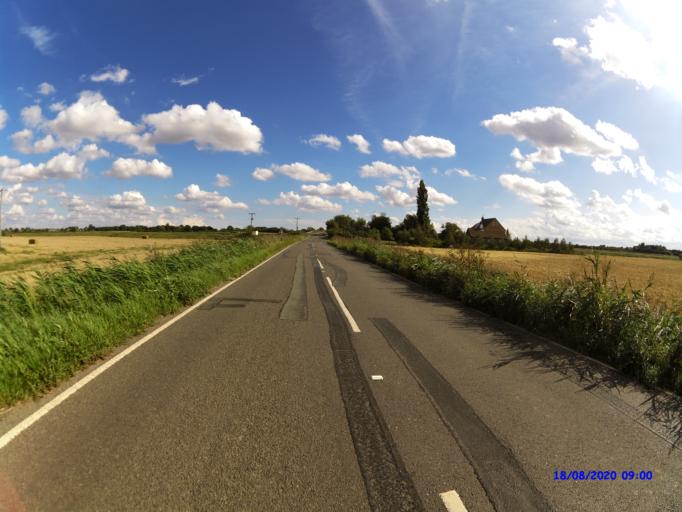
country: GB
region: England
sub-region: Cambridgeshire
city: Ramsey
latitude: 52.4742
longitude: -0.0963
